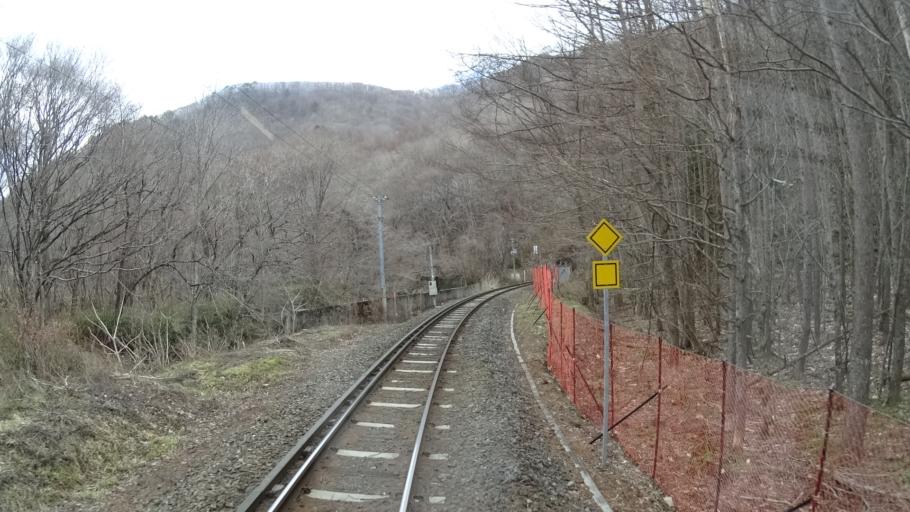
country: JP
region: Iwate
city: Tono
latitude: 39.2565
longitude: 141.6522
